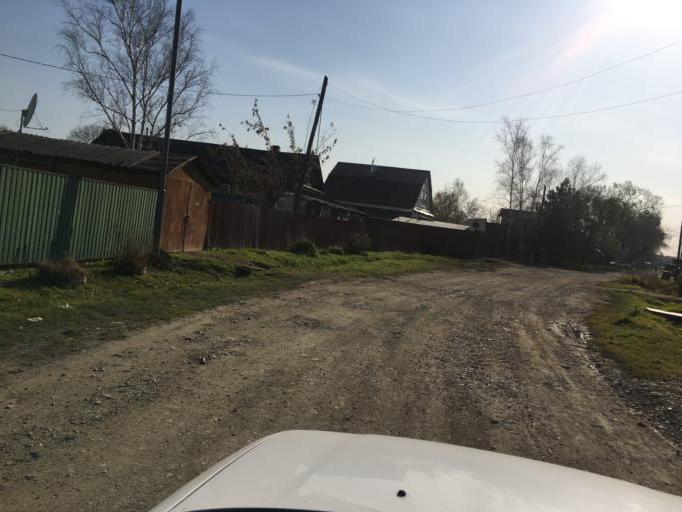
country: RU
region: Primorskiy
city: Dal'nerechensk
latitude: 45.9273
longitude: 133.7258
